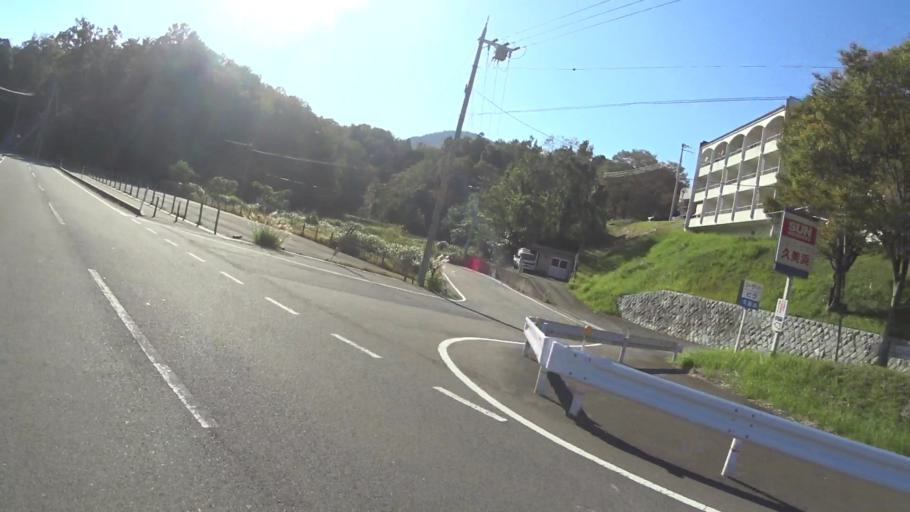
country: JP
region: Hyogo
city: Toyooka
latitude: 35.6363
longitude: 134.8894
